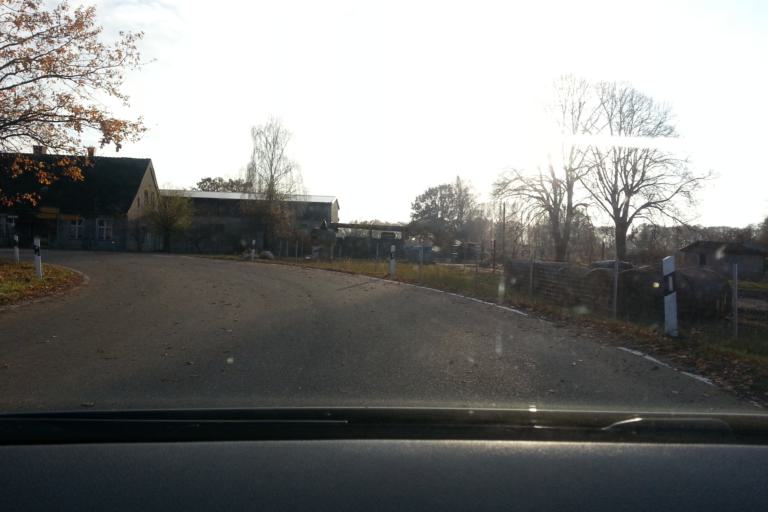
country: DE
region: Mecklenburg-Vorpommern
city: Ducherow
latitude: 53.6572
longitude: 13.7054
